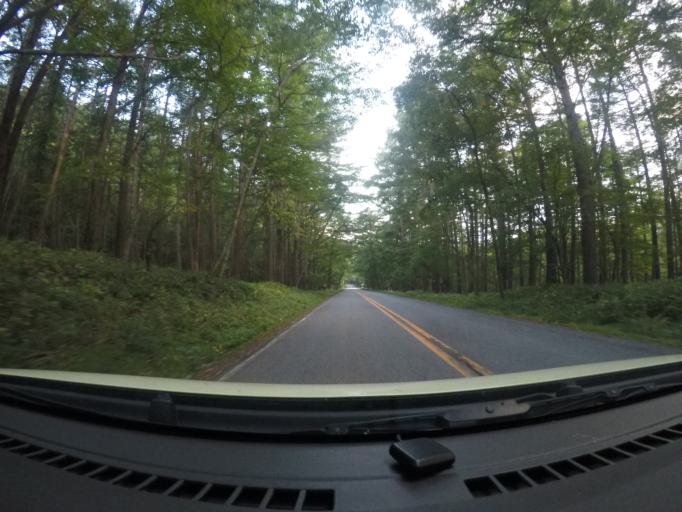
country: JP
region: Tochigi
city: Nikko
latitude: 36.7938
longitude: 139.4335
